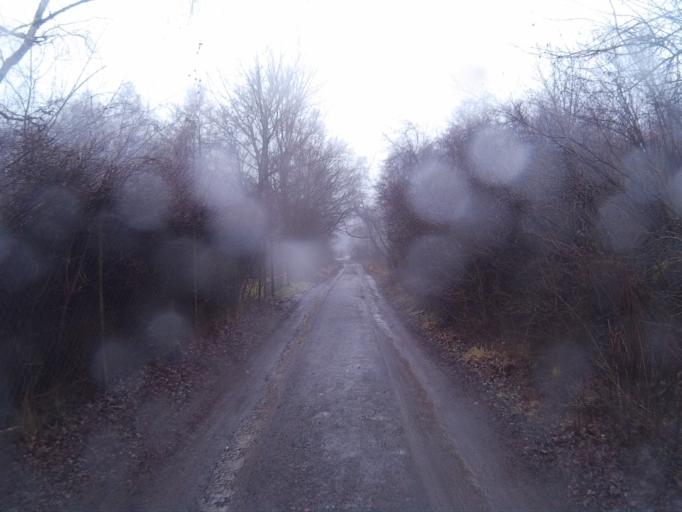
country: HU
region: Nograd
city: Somoskoujfalu
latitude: 48.1586
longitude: 19.8532
